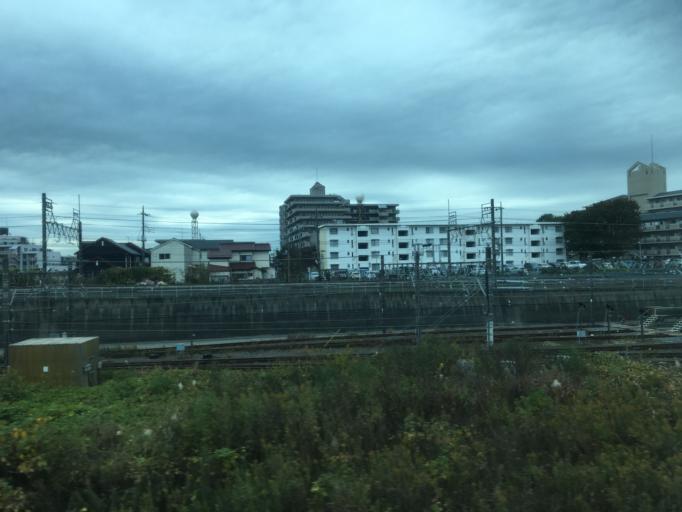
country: JP
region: Chiba
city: Abiko
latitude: 35.8734
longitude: 140.0351
